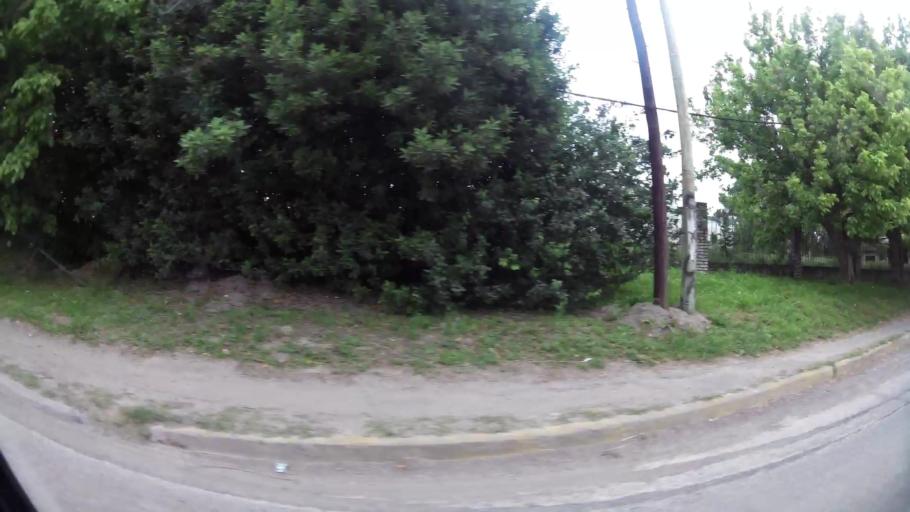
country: AR
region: Buenos Aires
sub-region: Partido de La Plata
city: La Plata
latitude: -34.9724
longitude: -58.0229
